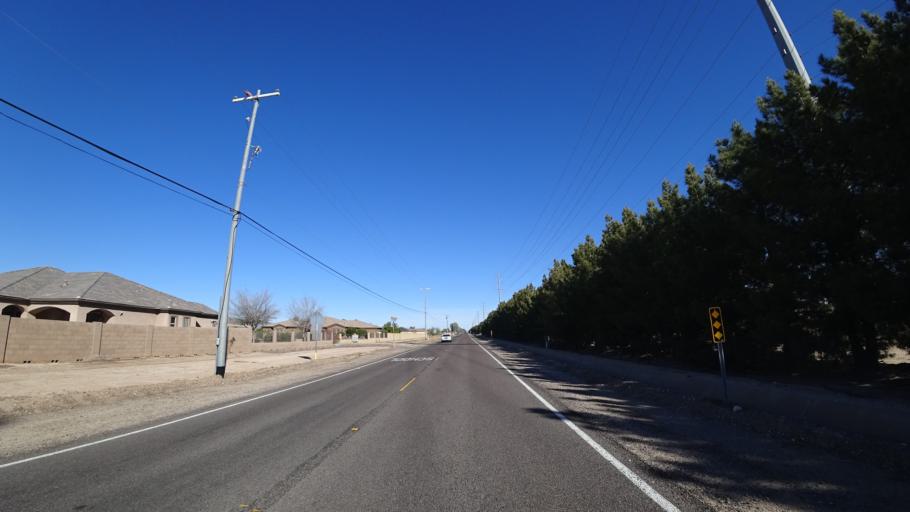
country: US
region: Arizona
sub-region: Maricopa County
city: Citrus Park
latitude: 33.4807
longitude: -112.4615
